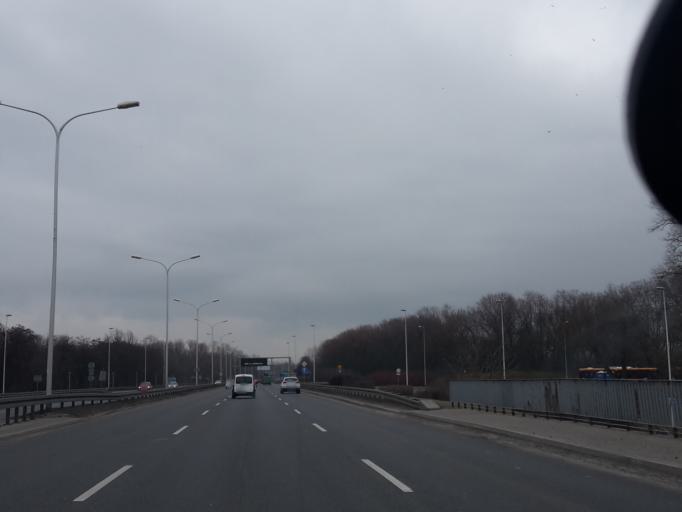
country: PL
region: Masovian Voivodeship
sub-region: Warszawa
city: Zoliborz
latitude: 52.2910
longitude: 20.9757
